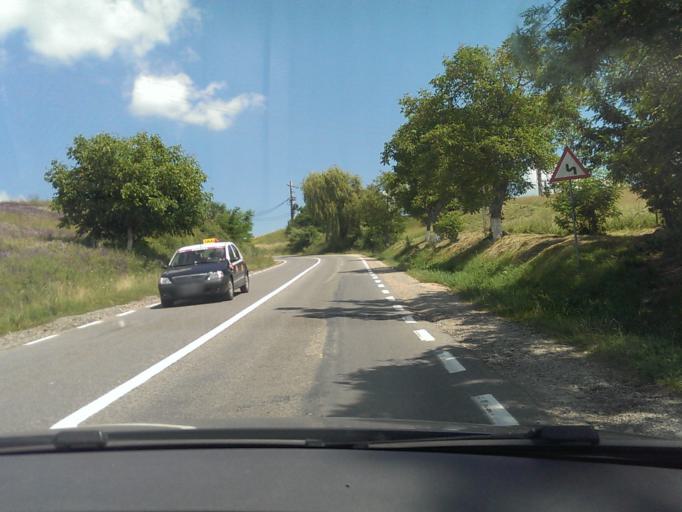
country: RO
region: Cluj
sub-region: Comuna Apahida
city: Apahida
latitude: 46.8004
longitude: 23.7631
